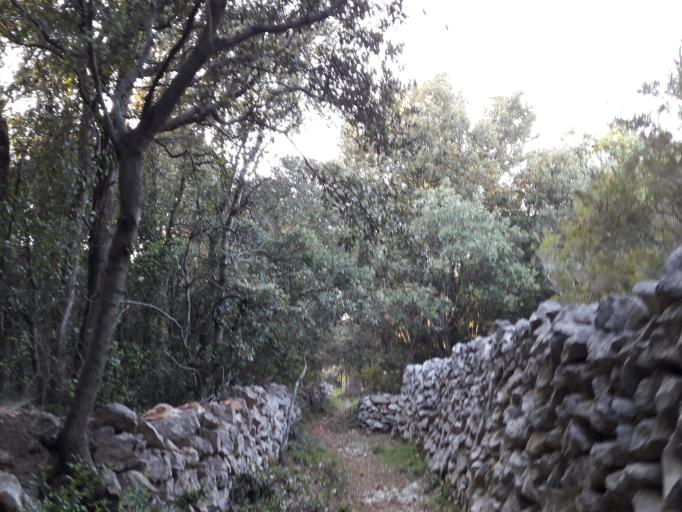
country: HR
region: Licko-Senjska
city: Novalja
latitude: 44.3636
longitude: 14.6958
